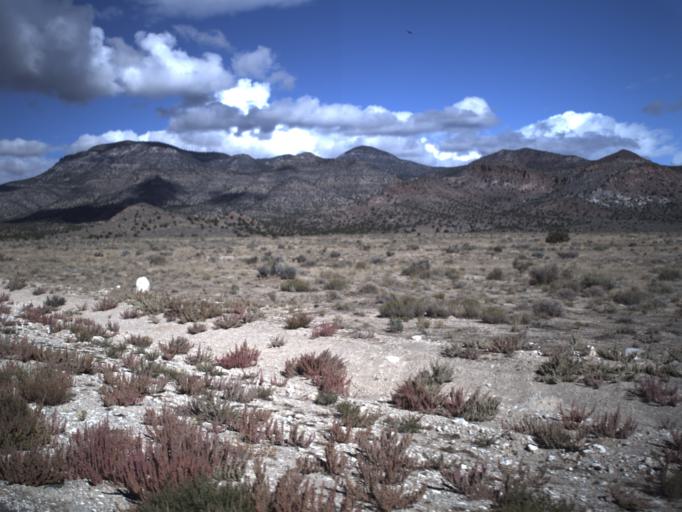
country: US
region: Utah
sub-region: Beaver County
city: Milford
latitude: 38.4975
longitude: -113.4900
